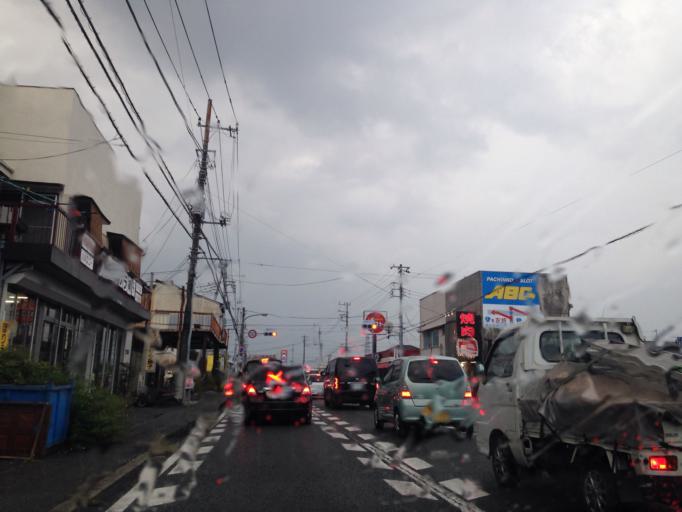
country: JP
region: Shizuoka
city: Mishima
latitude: 35.0961
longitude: 138.9259
